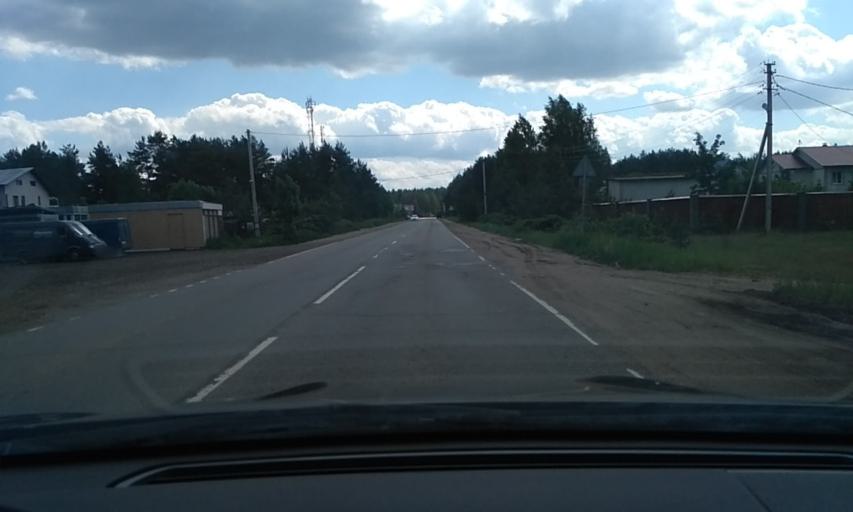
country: RU
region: Leningrad
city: Imeni Sverdlova
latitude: 59.8627
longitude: 30.6712
